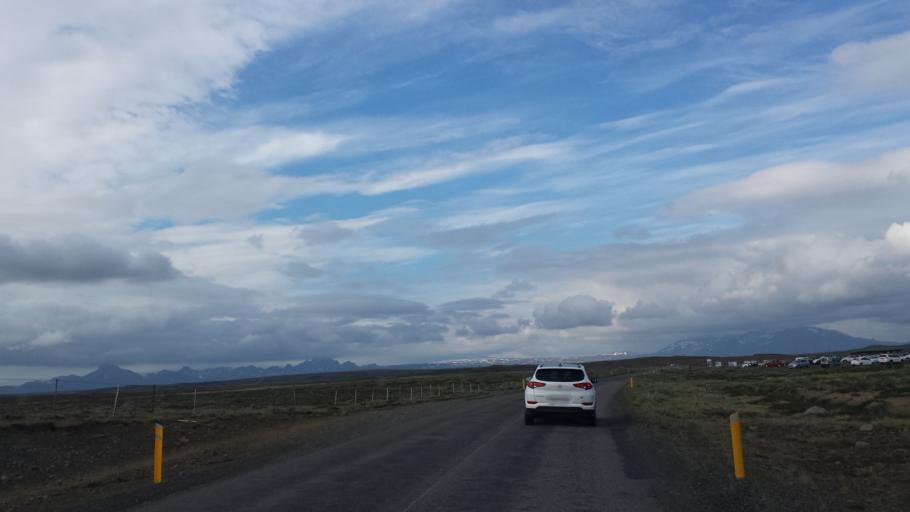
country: IS
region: South
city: Vestmannaeyjar
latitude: 64.3238
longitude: -20.1337
